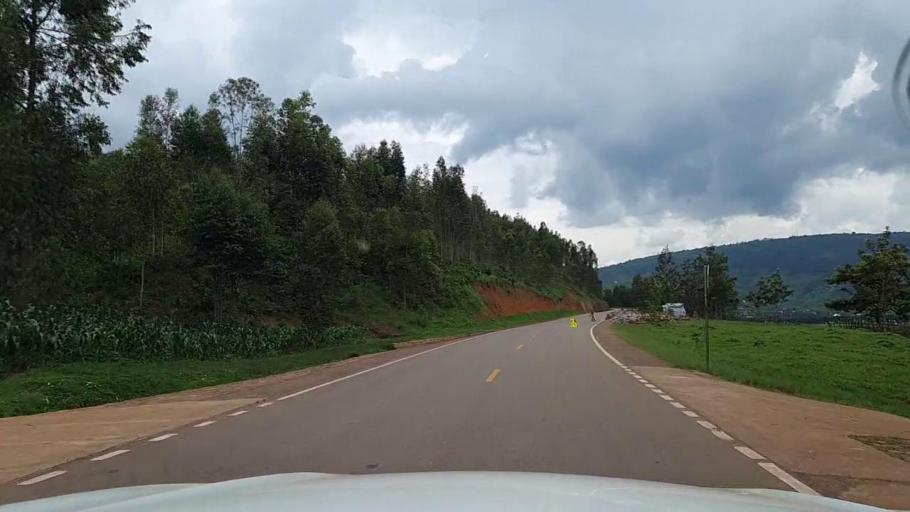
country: RW
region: Kigali
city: Kigali
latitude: -1.7924
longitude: 30.1281
